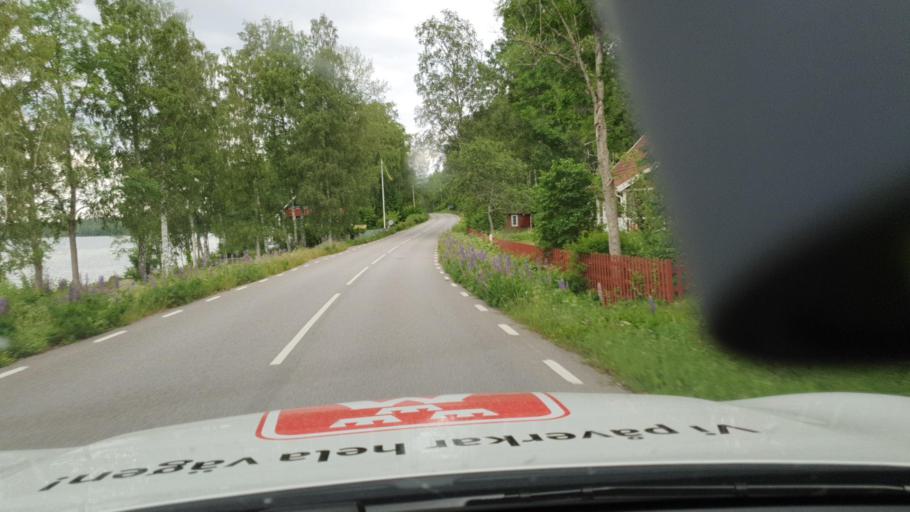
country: SE
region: Vaestra Goetaland
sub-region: Karlsborgs Kommun
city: Karlsborg
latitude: 58.7603
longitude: 14.5162
